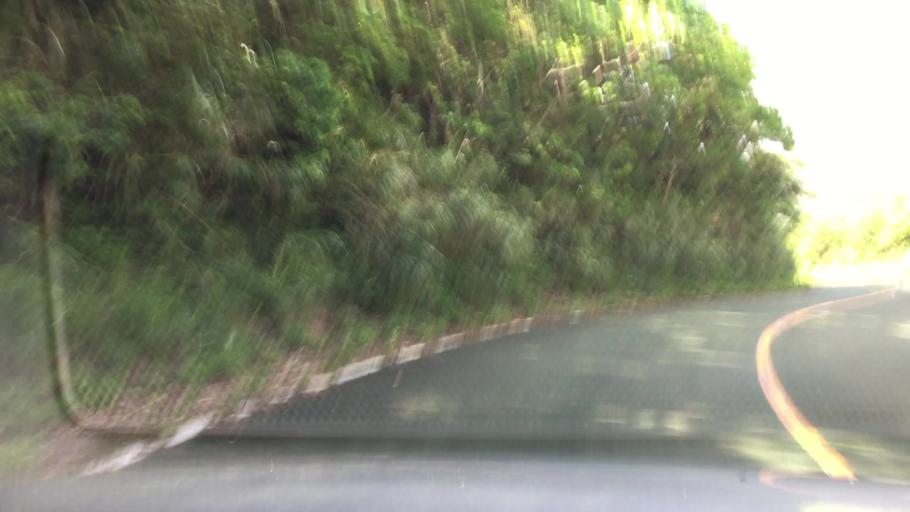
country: JP
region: Okinawa
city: Ishigaki
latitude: 24.3842
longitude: 124.1699
